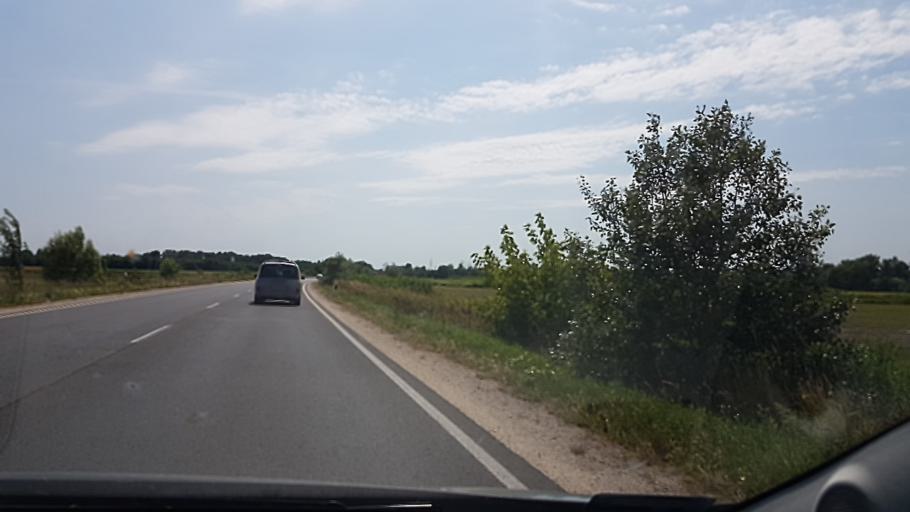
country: HU
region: Pest
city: Taksony
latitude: 47.3139
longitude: 19.0895
